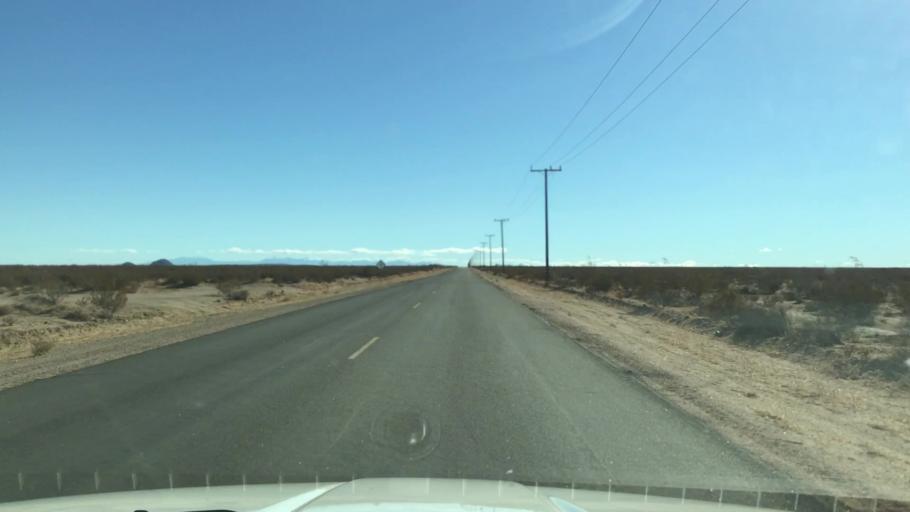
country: US
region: California
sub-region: Kern County
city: California City
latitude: 35.1972
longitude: -117.9859
